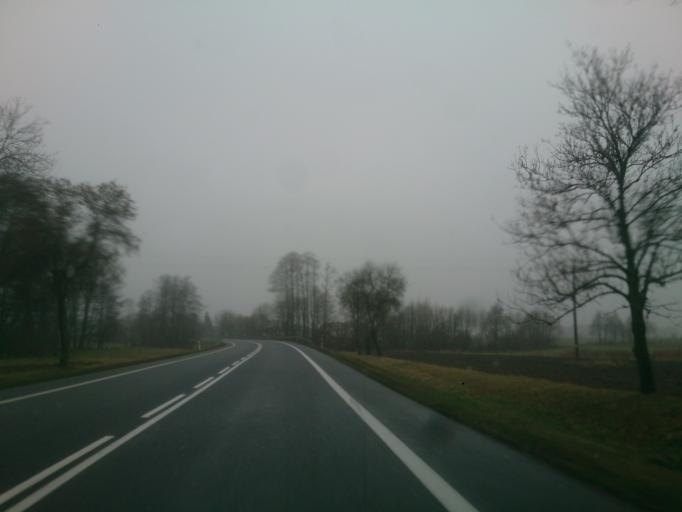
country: PL
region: Masovian Voivodeship
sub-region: Powiat sierpecki
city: Rosciszewo
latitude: 52.8228
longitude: 19.7747
